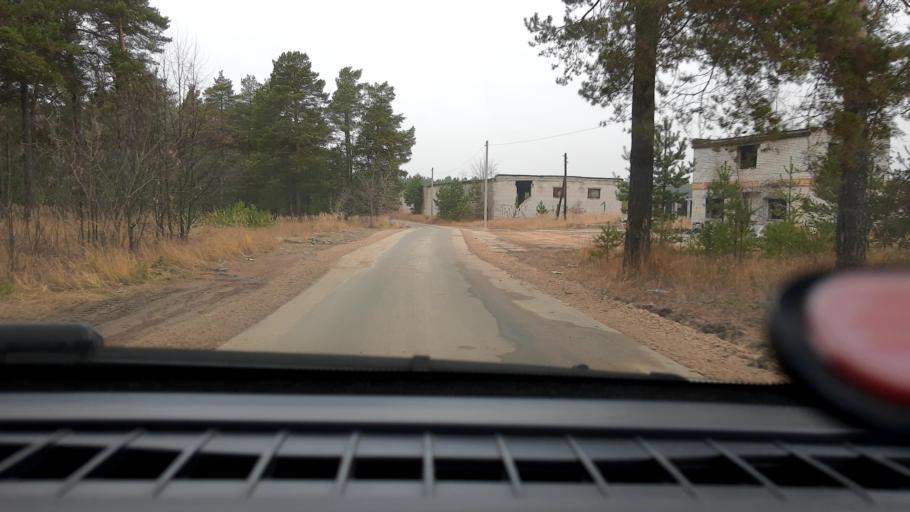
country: RU
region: Nizjnij Novgorod
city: Lukino
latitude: 56.3900
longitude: 43.7175
